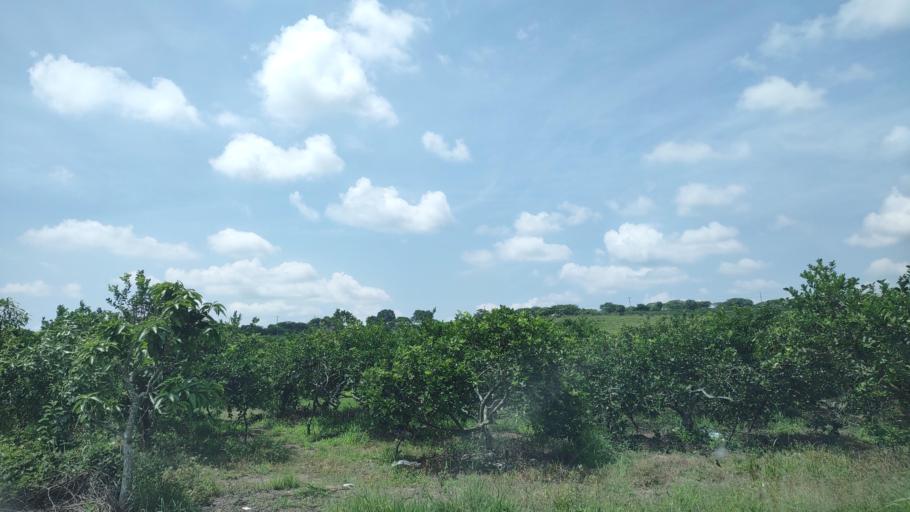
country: MX
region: Veracruz
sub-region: Emiliano Zapata
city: Dos Rios
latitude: 19.4660
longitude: -96.7978
